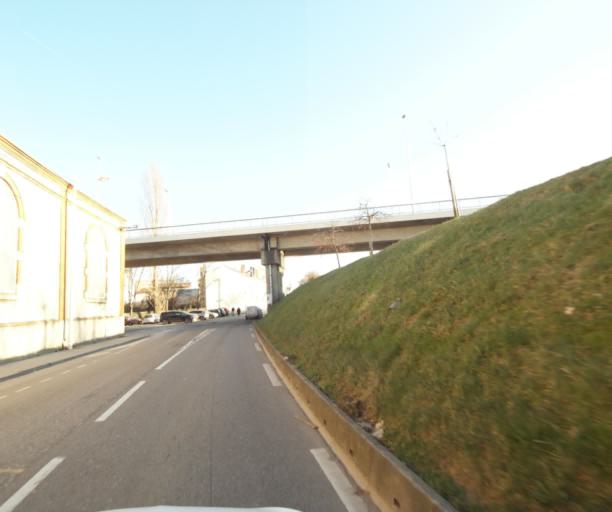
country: FR
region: Lorraine
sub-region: Departement de Meurthe-et-Moselle
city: Malzeville
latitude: 48.7016
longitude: 6.1879
